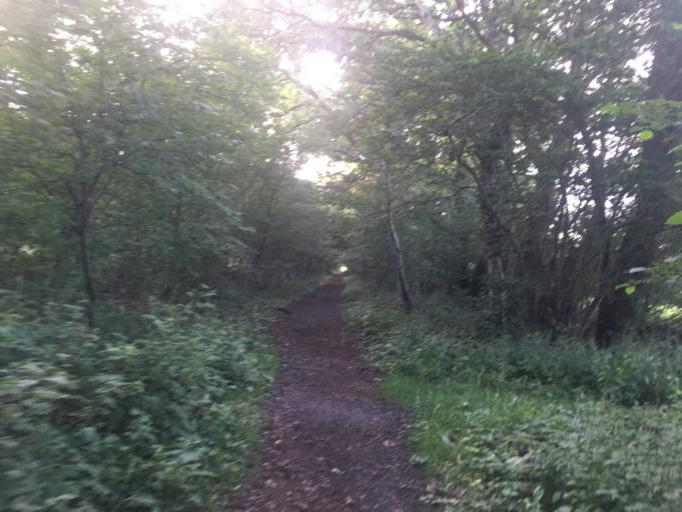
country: NL
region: Drenthe
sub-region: Gemeente Westerveld
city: Dwingeloo
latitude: 52.8636
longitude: 6.3102
